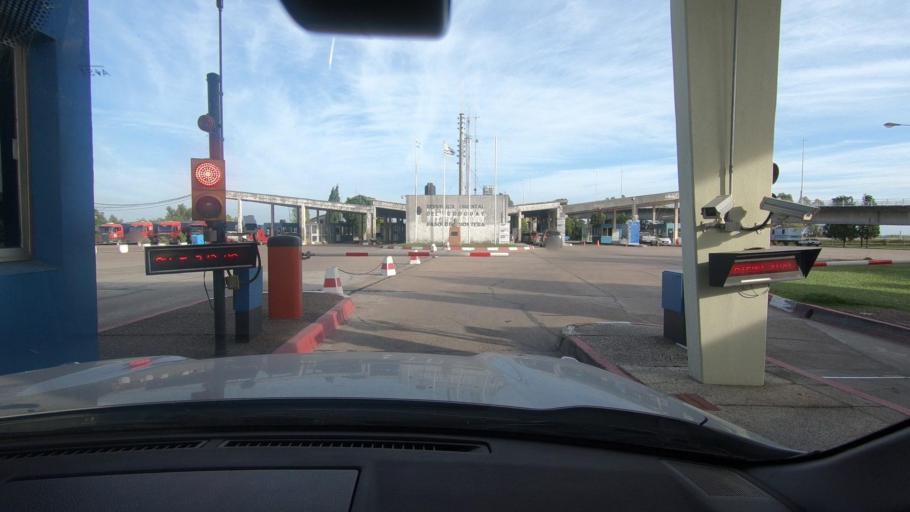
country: AR
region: Entre Rios
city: Colon
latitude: -32.2534
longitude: -58.1406
